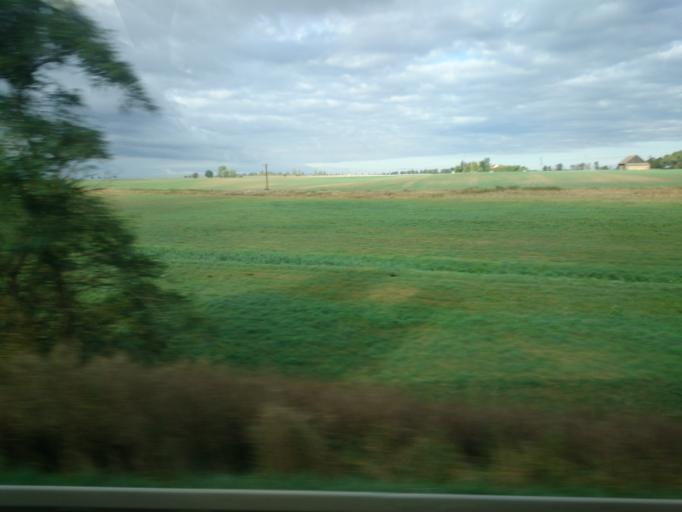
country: DE
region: Mecklenburg-Vorpommern
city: Pasewalk
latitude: 53.5096
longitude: 13.9762
